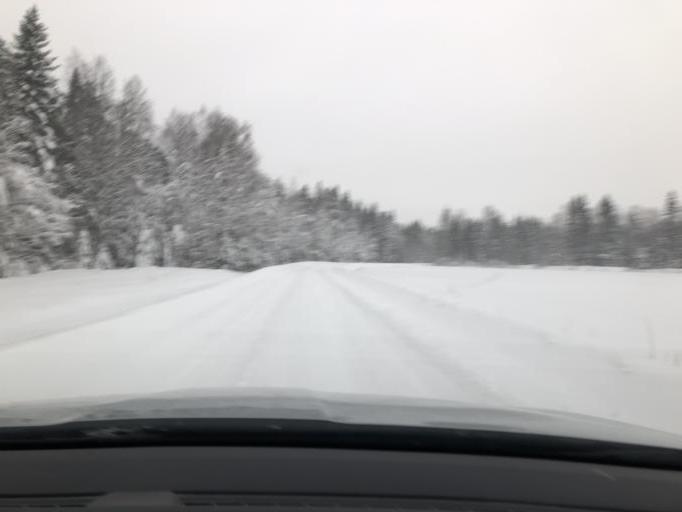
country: SE
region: Vaesterbotten
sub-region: Umea Kommun
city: Saevar
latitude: 63.9416
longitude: 20.7113
